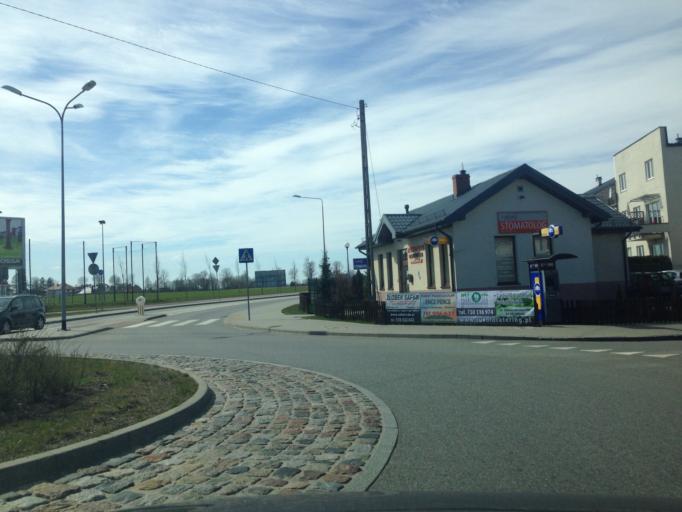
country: PL
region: Pomeranian Voivodeship
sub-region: Gdynia
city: Wielki Kack
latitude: 54.4985
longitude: 18.4388
